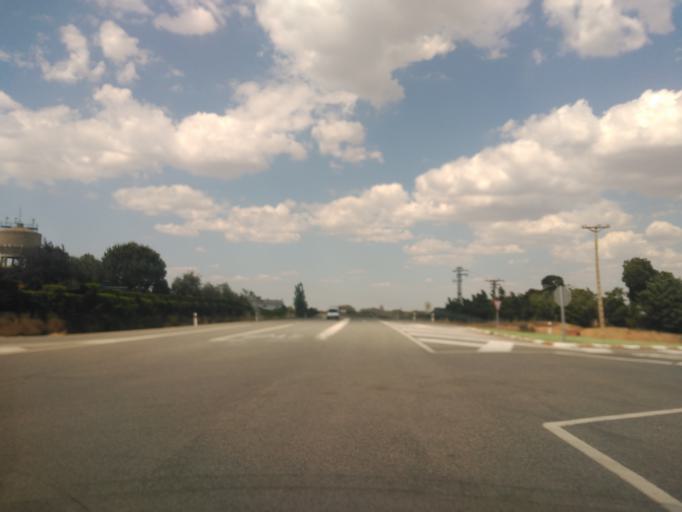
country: ES
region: Castille and Leon
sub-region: Provincia de Salamanca
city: Martinamor
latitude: 40.8102
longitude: -5.6307
